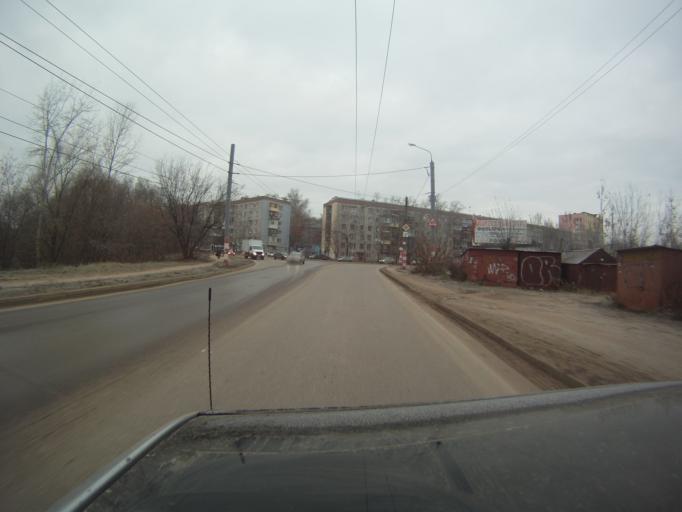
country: RU
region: Nizjnij Novgorod
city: Afonino
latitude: 56.2898
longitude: 44.0527
